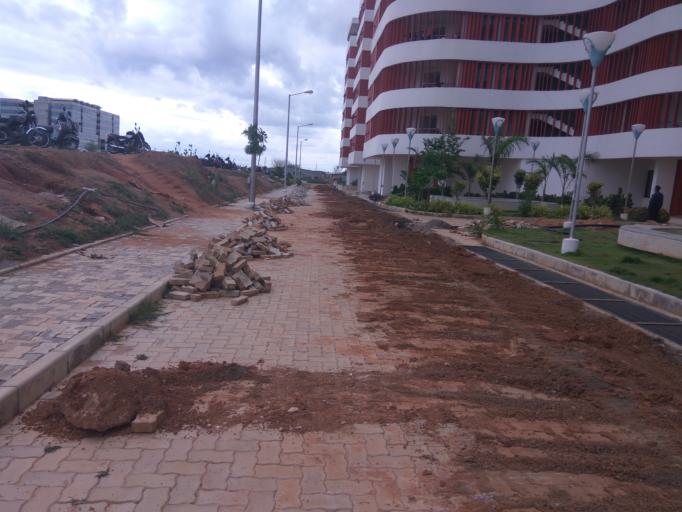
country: IN
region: Telangana
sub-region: Medak
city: Sangareddi
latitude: 17.5971
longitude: 78.1263
